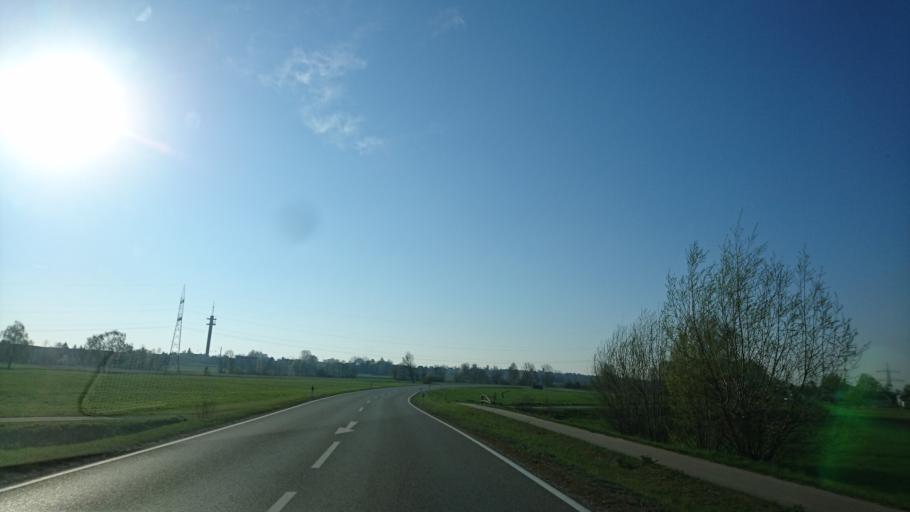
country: DE
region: Bavaria
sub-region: Swabia
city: Gablingen
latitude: 48.4346
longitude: 10.8173
